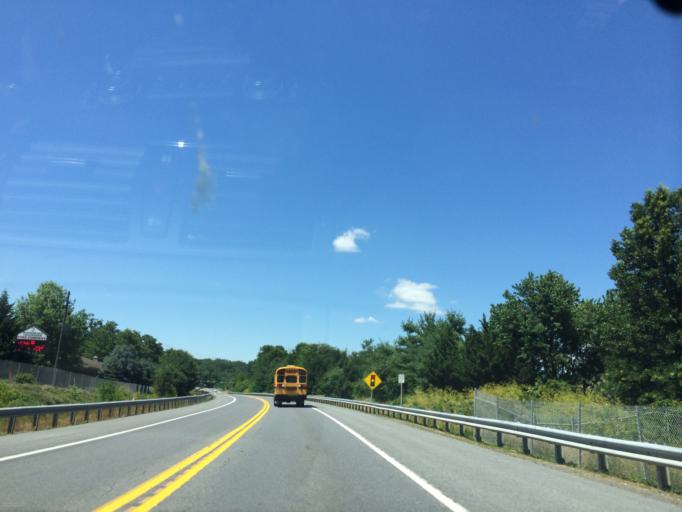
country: US
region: Maryland
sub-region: Frederick County
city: Woodsboro
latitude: 39.5342
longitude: -77.3113
